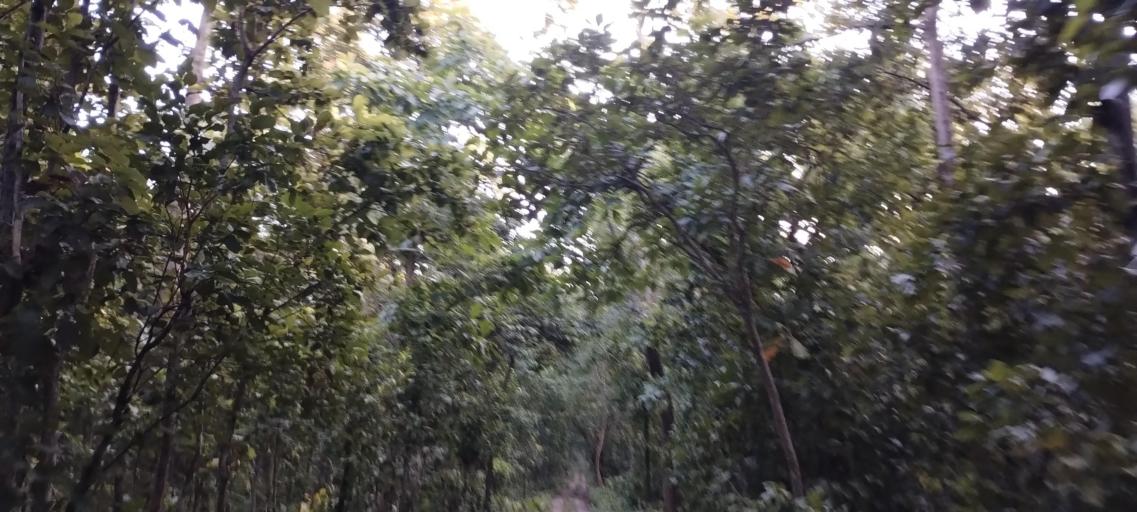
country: NP
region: Far Western
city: Tikapur
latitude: 28.4821
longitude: 81.2611
